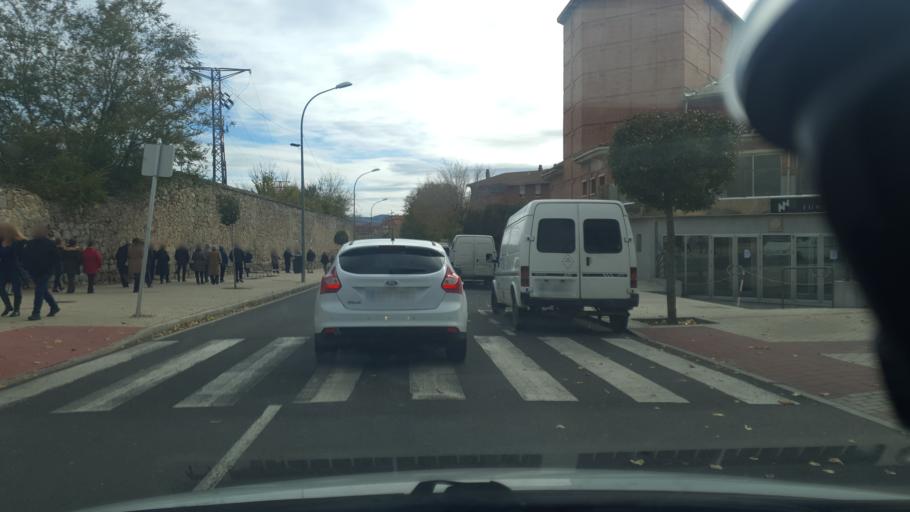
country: ES
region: Castille and Leon
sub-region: Provincia de Avila
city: Avila
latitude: 40.6493
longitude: -4.6887
